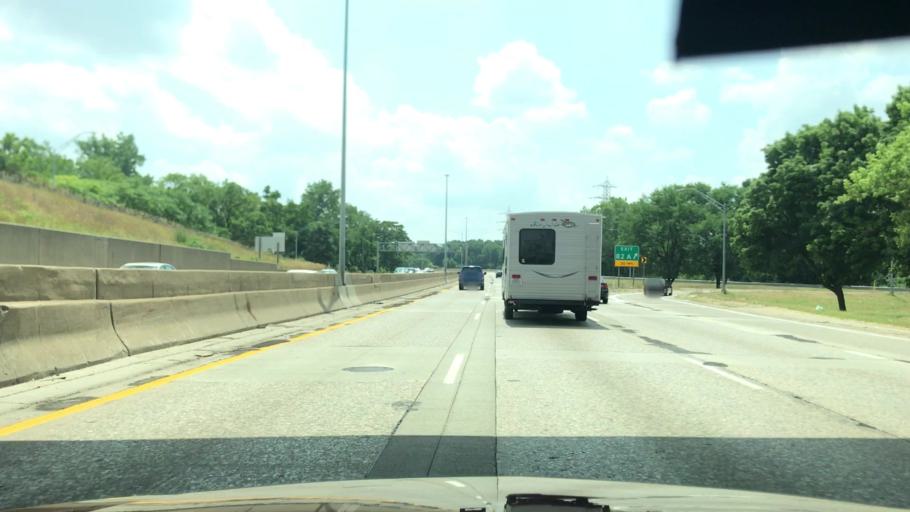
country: US
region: Michigan
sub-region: Kent County
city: Wyoming
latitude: 42.9278
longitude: -85.6818
